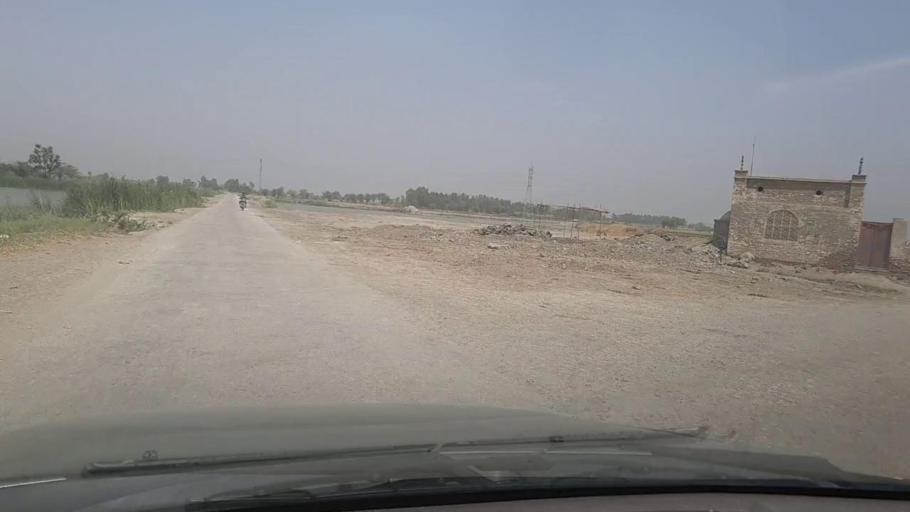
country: PK
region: Sindh
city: Madeji
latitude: 27.8259
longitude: 68.3943
